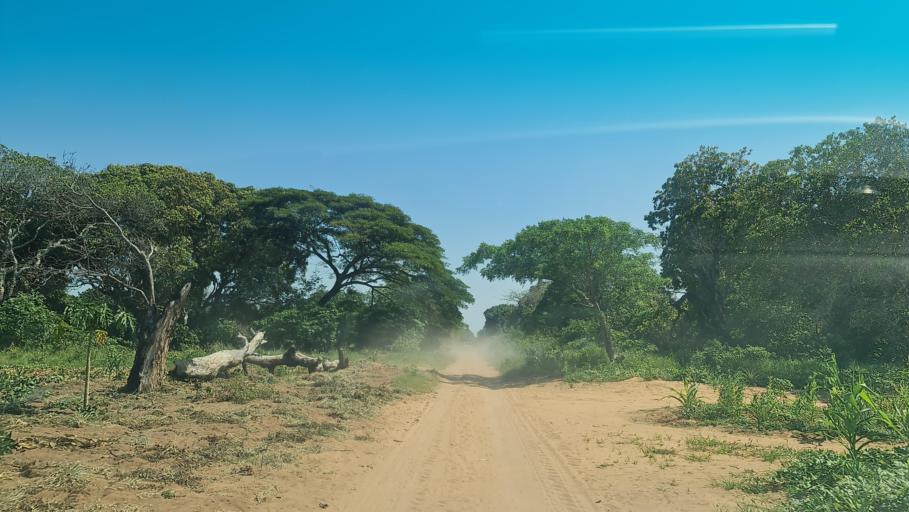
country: MZ
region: Gaza
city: Macia
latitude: -25.0811
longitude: 33.1005
